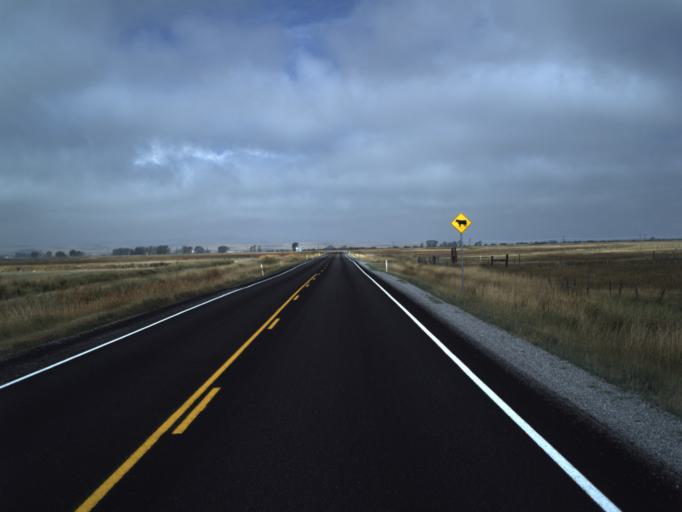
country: US
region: Utah
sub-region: Rich County
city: Randolph
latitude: 41.5039
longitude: -111.1248
